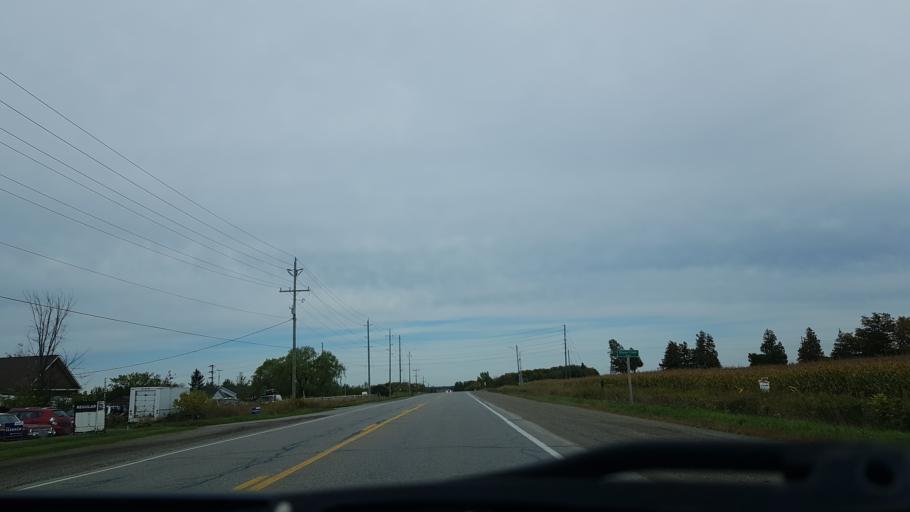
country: CA
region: Ontario
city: Orangeville
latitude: 43.8092
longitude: -80.0516
